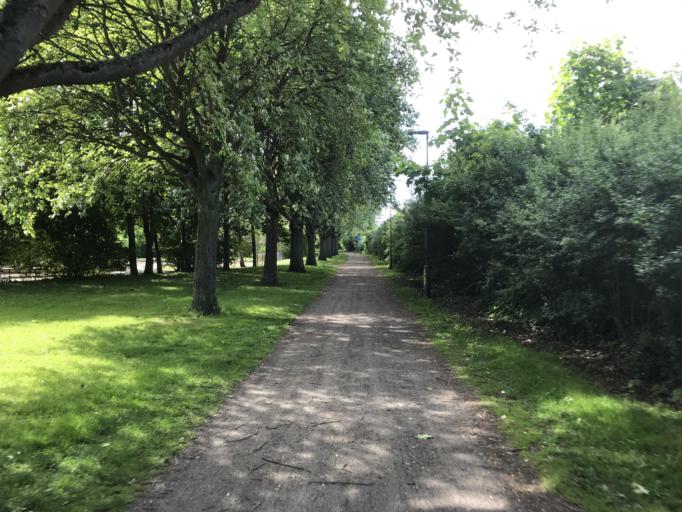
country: SE
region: Skane
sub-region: Malmo
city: Malmoe
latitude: 55.5675
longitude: 13.0285
